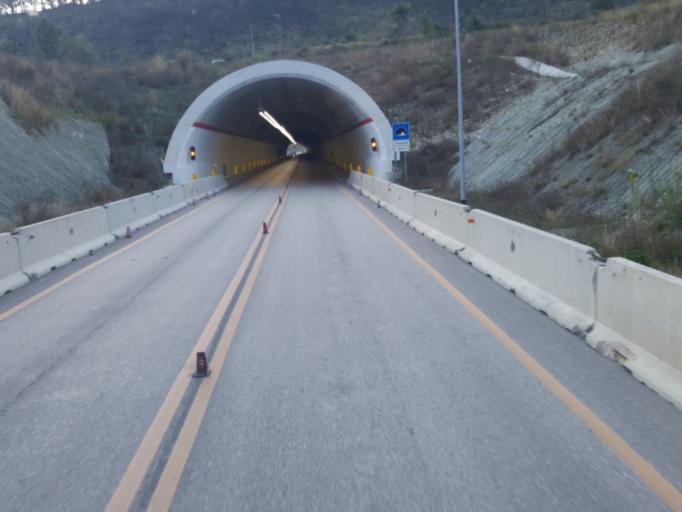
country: IT
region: Umbria
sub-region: Provincia di Perugia
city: Fossato di Vico
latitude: 43.3033
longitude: 12.8318
